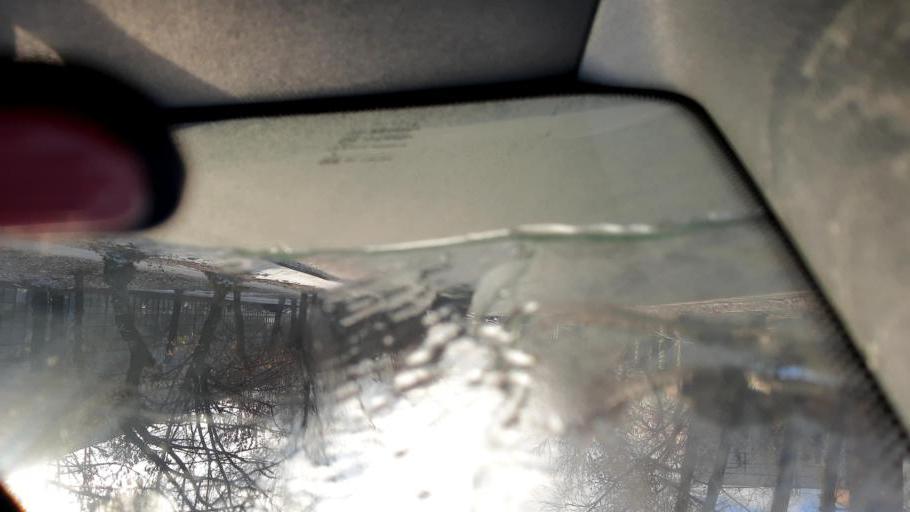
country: RU
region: Bashkortostan
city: Ufa
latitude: 54.8076
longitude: 56.0804
